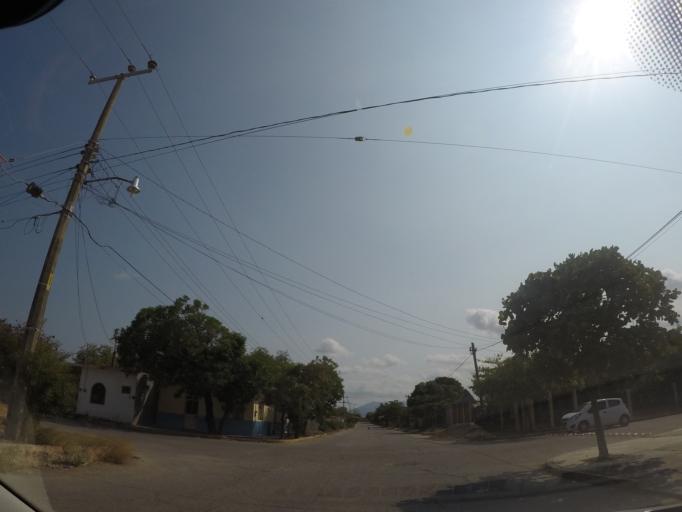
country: MX
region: Oaxaca
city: San Jeronimo Ixtepec
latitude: 16.5476
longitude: -95.0882
